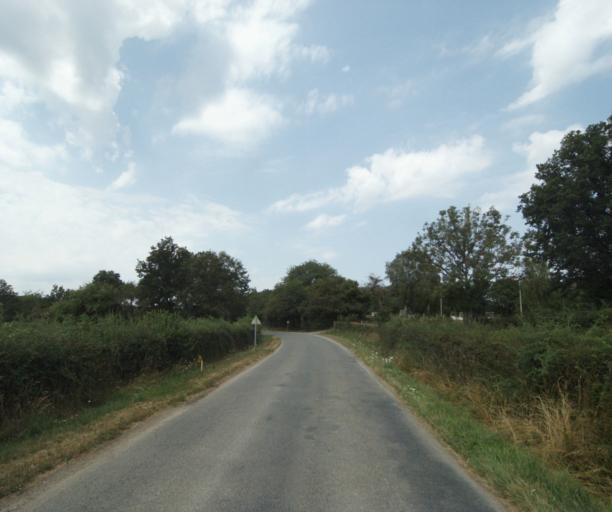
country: FR
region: Bourgogne
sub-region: Departement de Saone-et-Loire
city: Gueugnon
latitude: 46.5872
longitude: 4.0331
